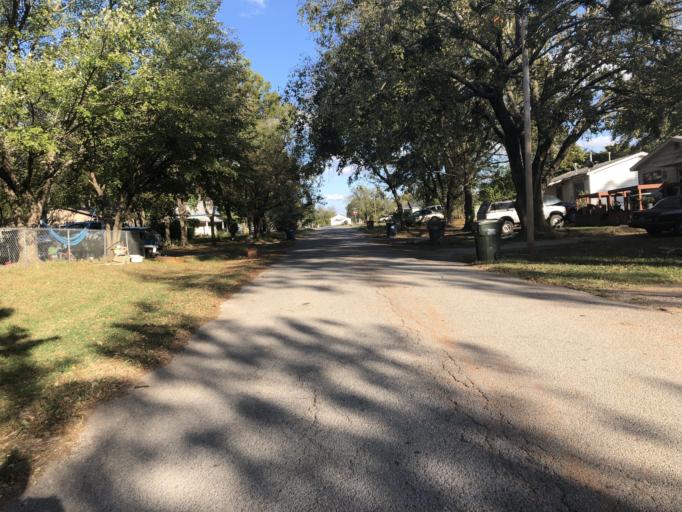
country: US
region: Oklahoma
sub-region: Pottawatomie County
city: Tecumseh
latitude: 35.2597
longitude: -96.9328
